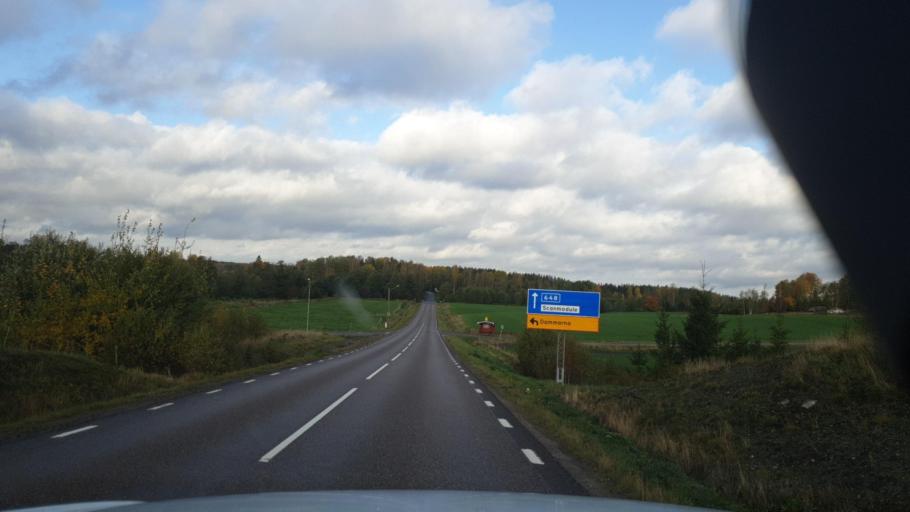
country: SE
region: Vaermland
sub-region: Arvika Kommun
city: Arvika
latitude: 59.5245
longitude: 12.6218
